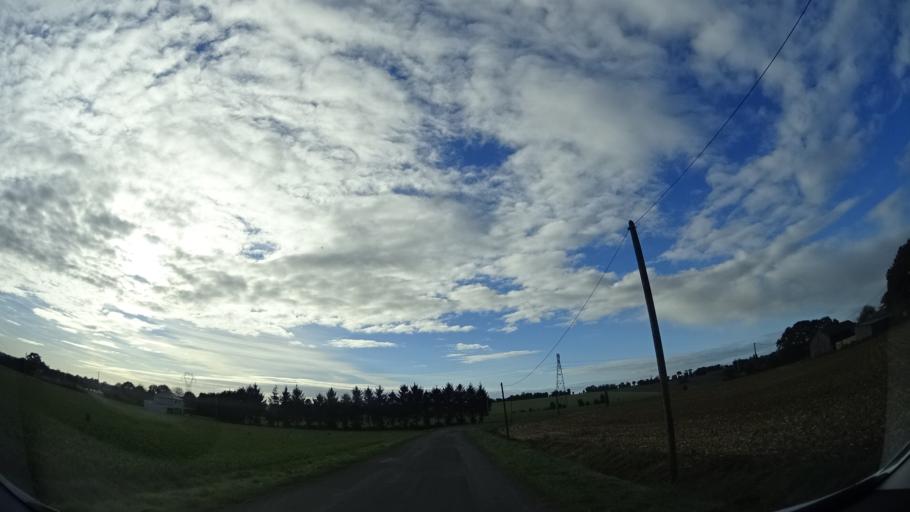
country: FR
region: Brittany
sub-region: Departement d'Ille-et-Vilaine
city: Geveze
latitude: 48.2033
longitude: -1.8064
